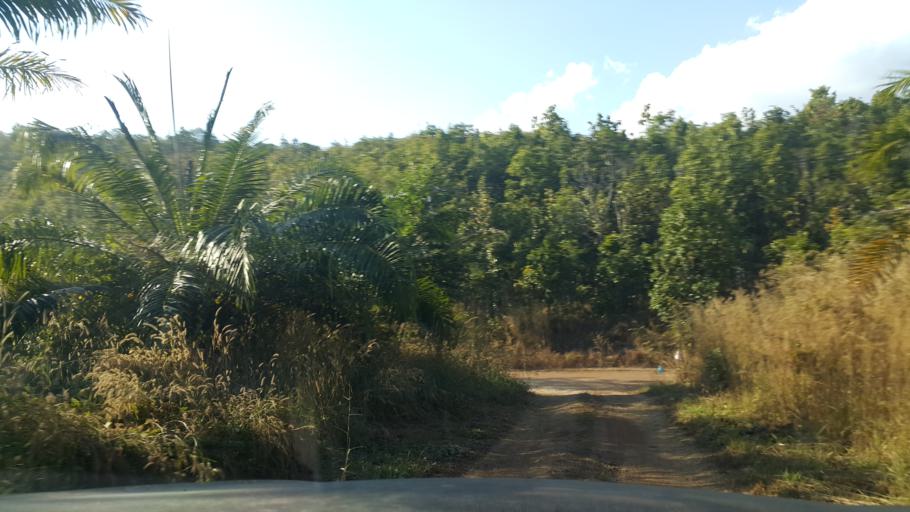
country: TH
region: Lamphun
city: Mae Tha
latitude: 18.5272
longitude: 99.1232
